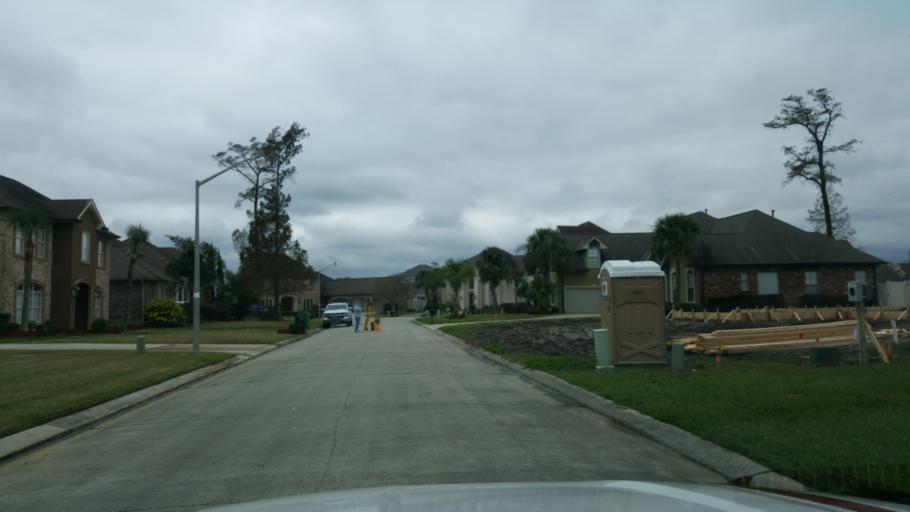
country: US
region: Louisiana
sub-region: Jefferson Parish
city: Woodmere
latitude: 29.8804
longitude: -90.0784
